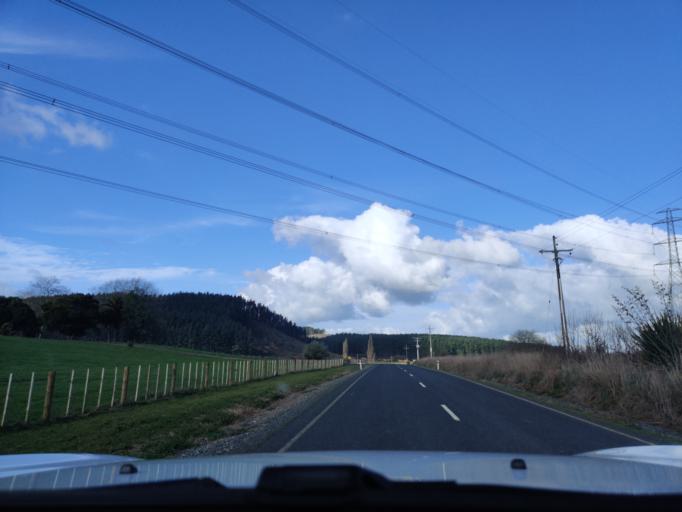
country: NZ
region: Waikato
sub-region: Waikato District
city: Te Kauwhata
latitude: -37.2906
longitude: 175.2213
